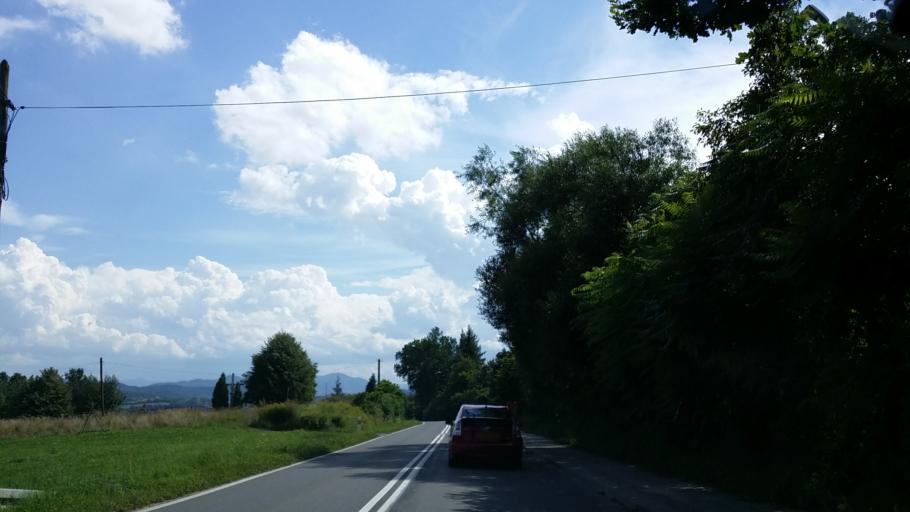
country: PL
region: Lesser Poland Voivodeship
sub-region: Powiat myslenicki
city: Dobczyce
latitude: 49.9063
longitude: 20.0972
